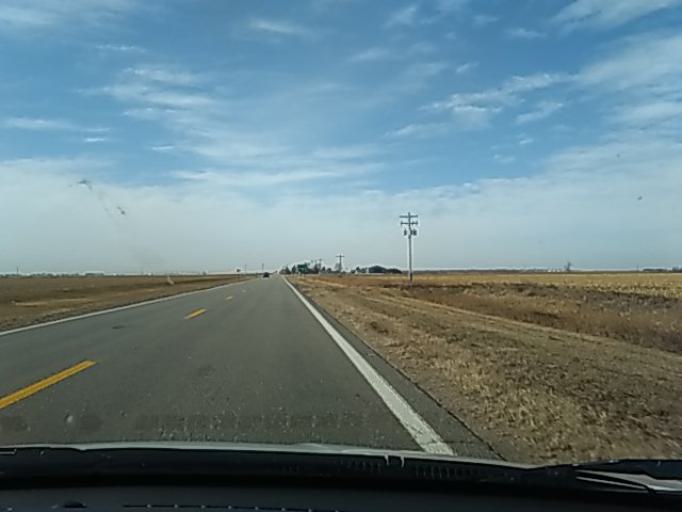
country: US
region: Nebraska
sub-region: Clay County
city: Clay Center
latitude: 40.4233
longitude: -98.0460
